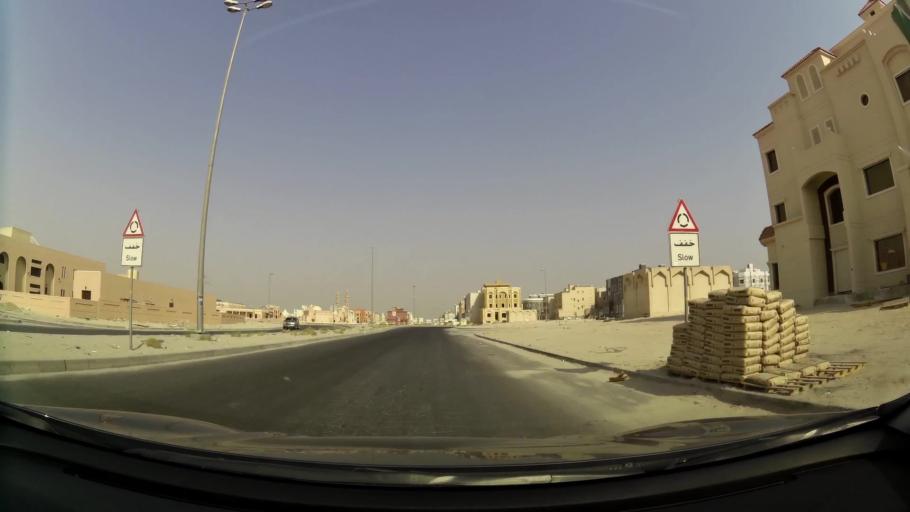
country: KW
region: Muhafazat al Jahra'
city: Al Jahra'
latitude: 29.3498
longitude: 47.7719
